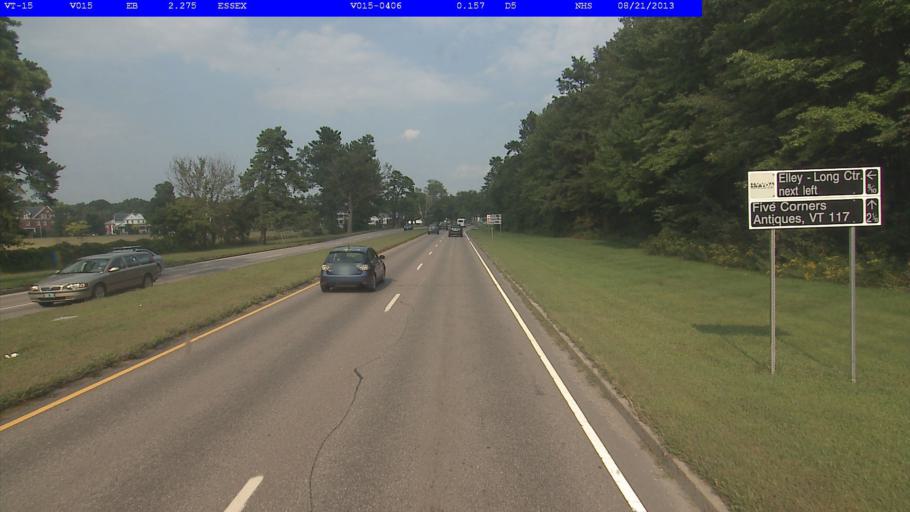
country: US
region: Vermont
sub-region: Chittenden County
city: Essex Junction
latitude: 44.5029
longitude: -73.1466
